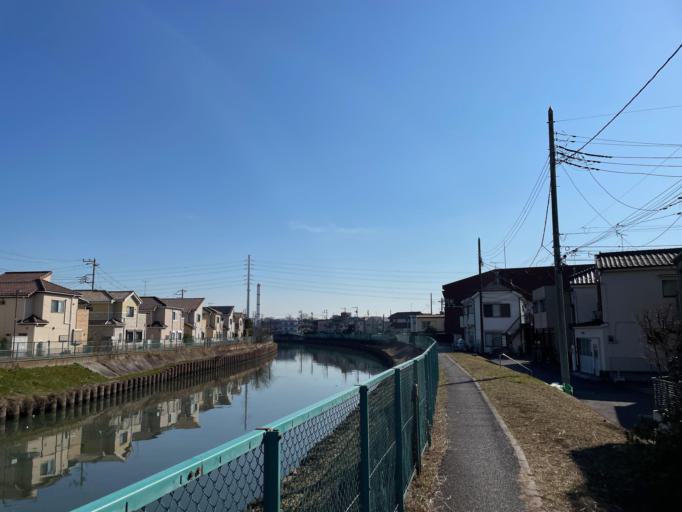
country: JP
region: Saitama
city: Soka
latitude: 35.8074
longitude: 139.7803
